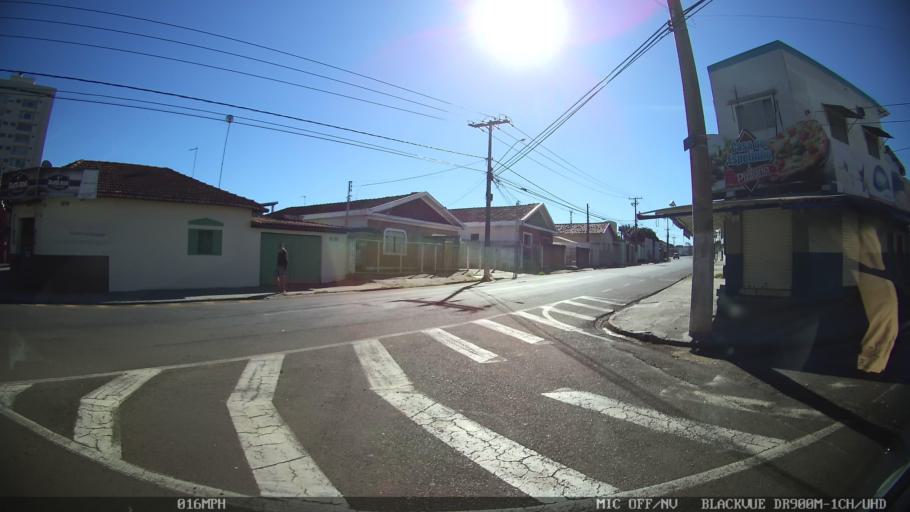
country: BR
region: Sao Paulo
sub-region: Franca
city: Franca
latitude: -20.5481
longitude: -47.3919
